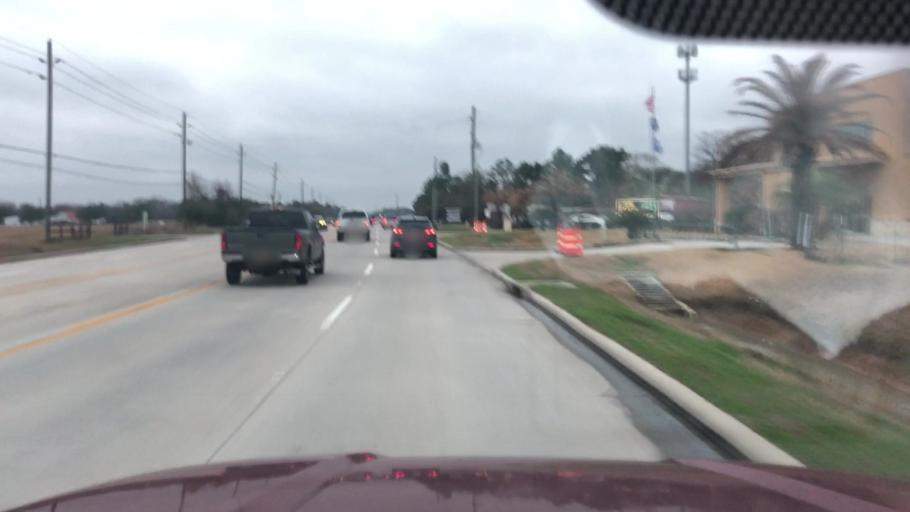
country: US
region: Texas
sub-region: Harris County
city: Tomball
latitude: 30.0493
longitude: -95.5391
